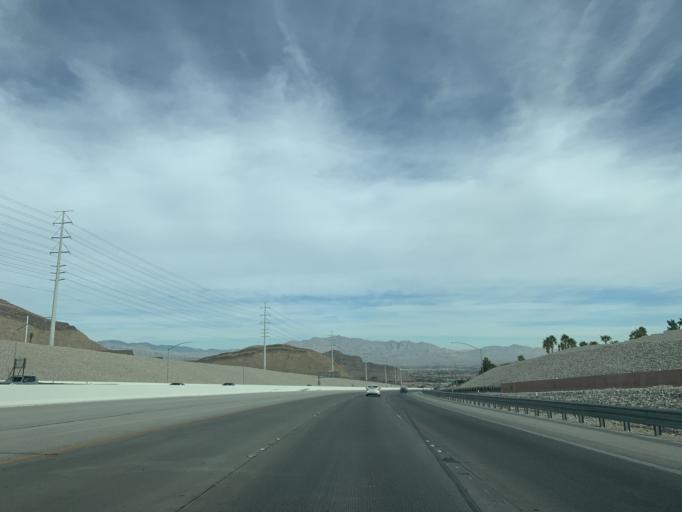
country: US
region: Nevada
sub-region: Clark County
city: Summerlin South
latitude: 36.2091
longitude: -115.3385
